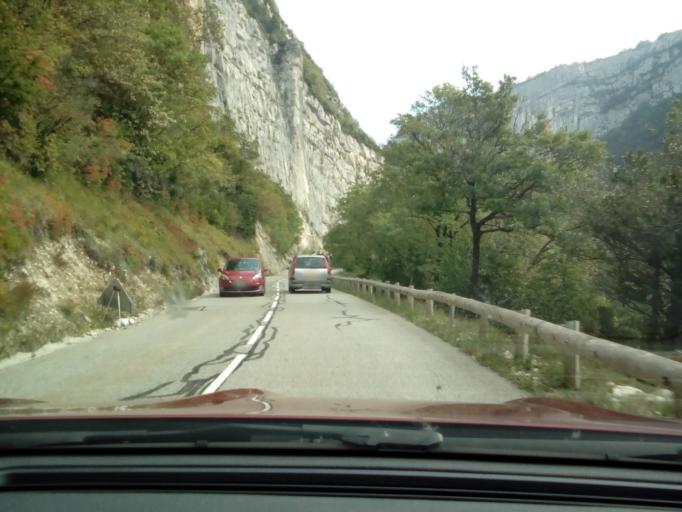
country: FR
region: Rhone-Alpes
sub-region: Departement de la Drome
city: Saint-Laurent-en-Royans
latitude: 45.0139
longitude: 5.4060
